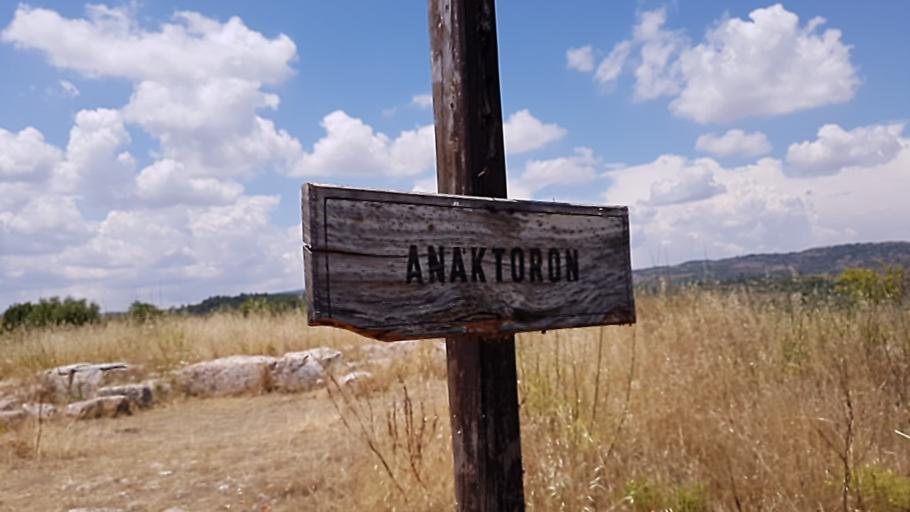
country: IT
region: Sicily
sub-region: Provincia di Siracusa
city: Sortino
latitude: 37.1343
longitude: 15.0257
